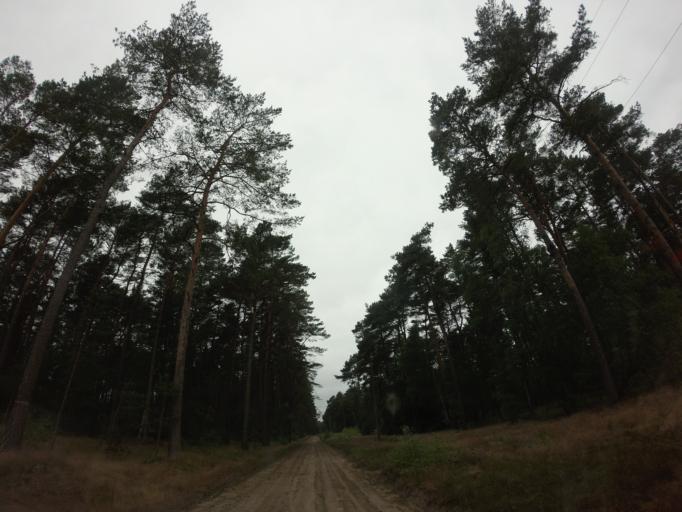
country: PL
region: West Pomeranian Voivodeship
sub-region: Powiat choszczenski
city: Drawno
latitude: 53.1417
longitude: 15.7254
